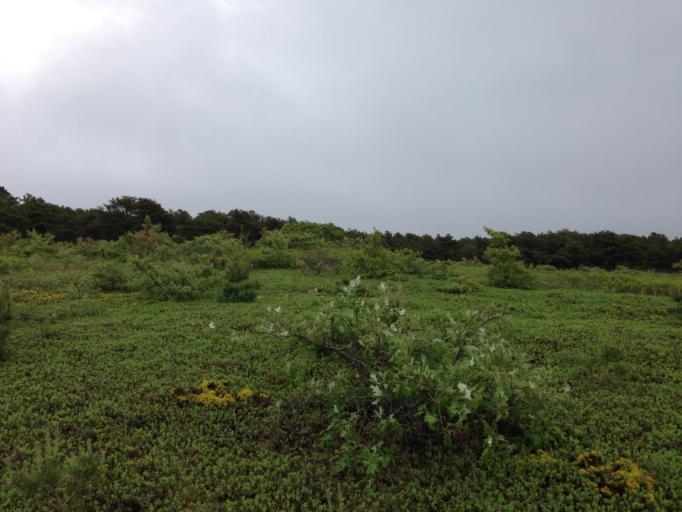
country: US
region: Massachusetts
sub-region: Barnstable County
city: North Eastham
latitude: 41.8854
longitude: -69.9959
